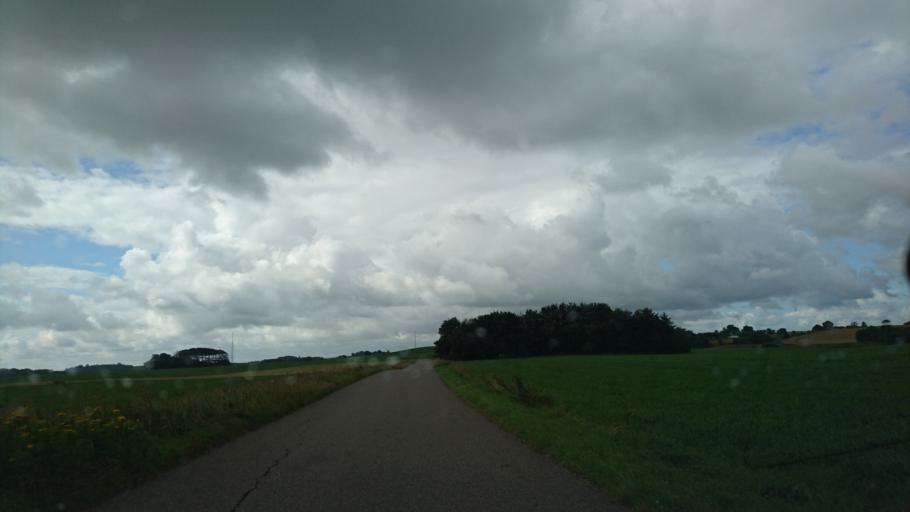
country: DK
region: North Denmark
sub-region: Hjorring Kommune
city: Tars
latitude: 57.3728
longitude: 10.2117
